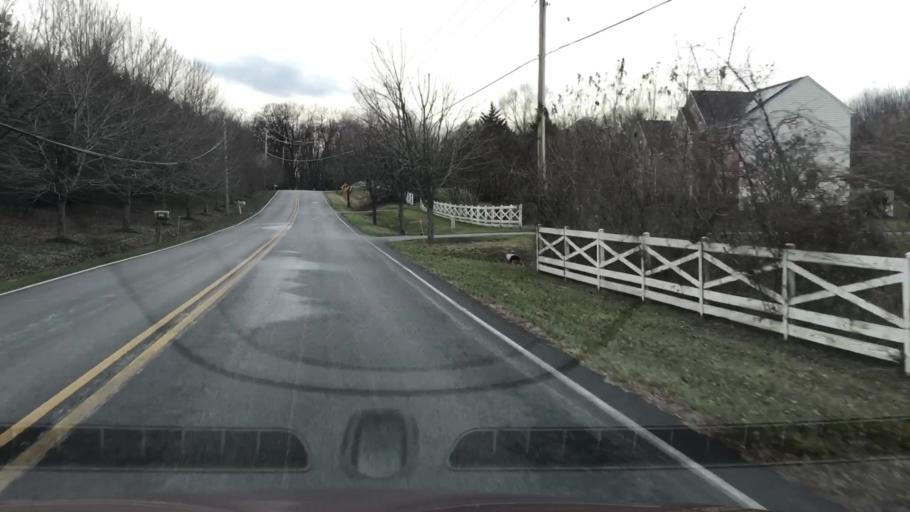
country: US
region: Maryland
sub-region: Howard County
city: Fulton
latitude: 39.1687
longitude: -76.9204
